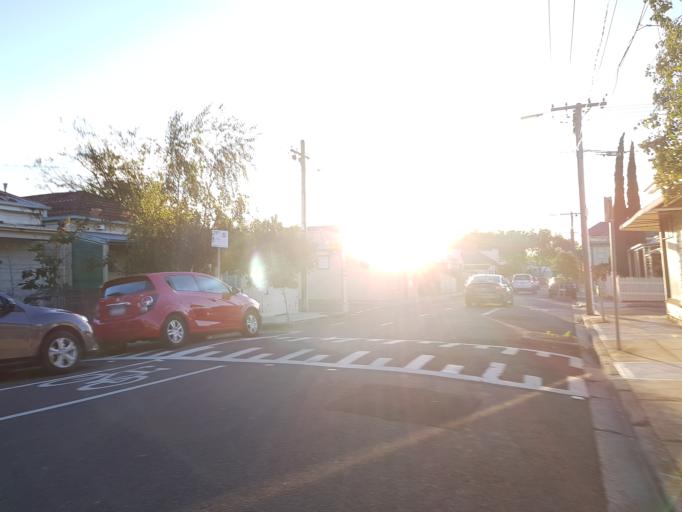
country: AU
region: Victoria
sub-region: Maribyrnong
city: Seddon
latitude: -37.8014
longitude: 144.8913
